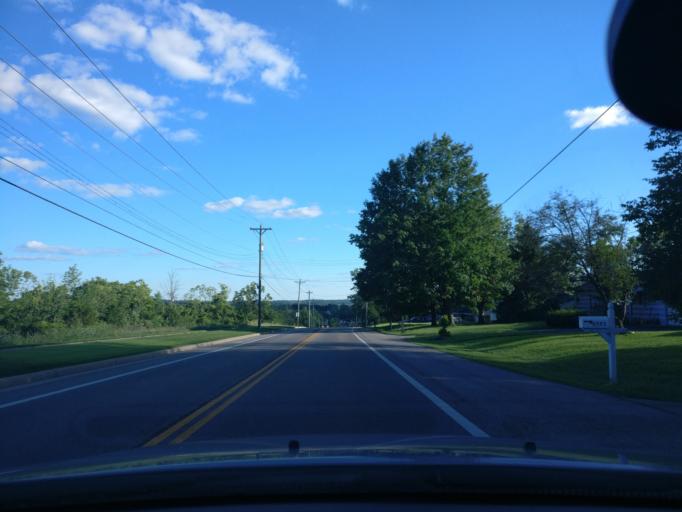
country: US
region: Ohio
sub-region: Warren County
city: Springboro
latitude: 39.5665
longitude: -84.2522
